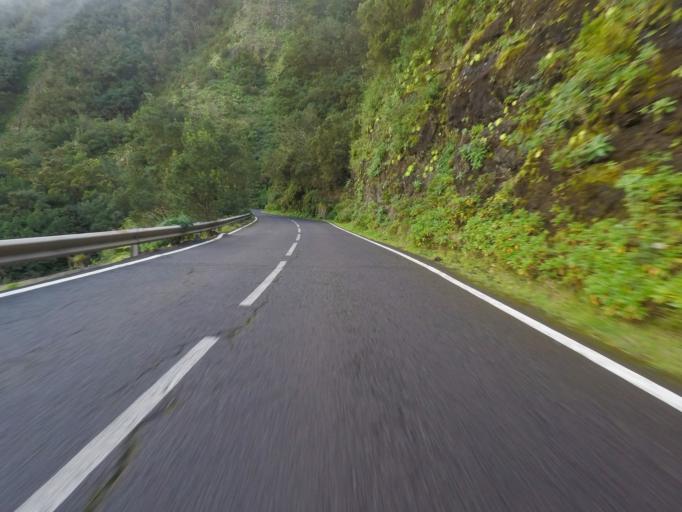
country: ES
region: Canary Islands
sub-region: Provincia de Santa Cruz de Tenerife
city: Hermigua
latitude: 28.1252
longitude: -17.2060
